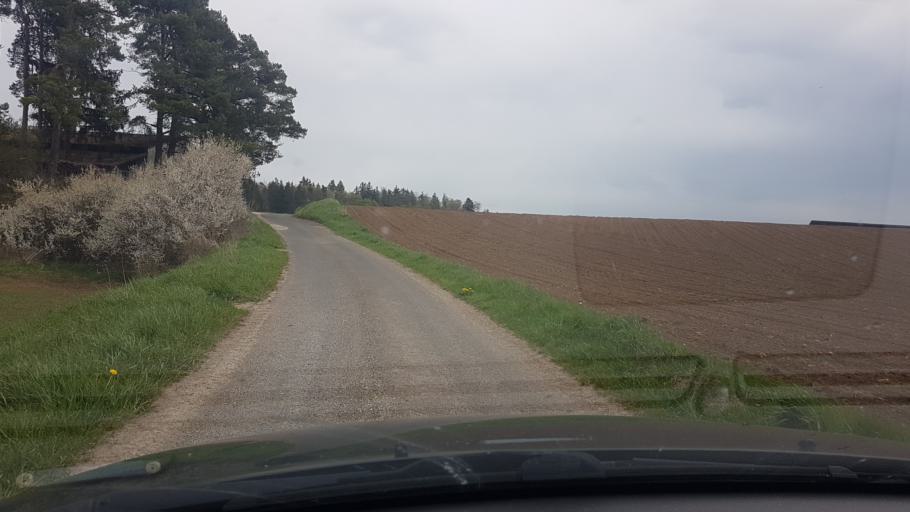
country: DE
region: Bavaria
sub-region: Upper Franconia
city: Wattendorf
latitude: 50.0121
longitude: 11.1525
